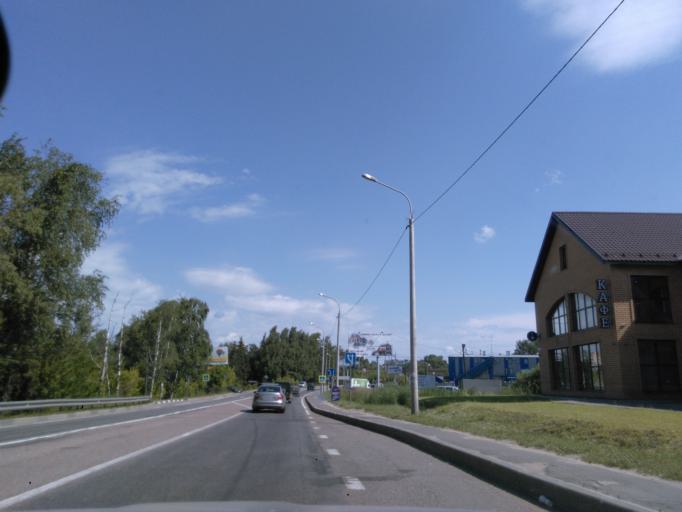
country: RU
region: Moskovskaya
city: Solnechnogorsk
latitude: 56.1856
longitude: 36.9620
